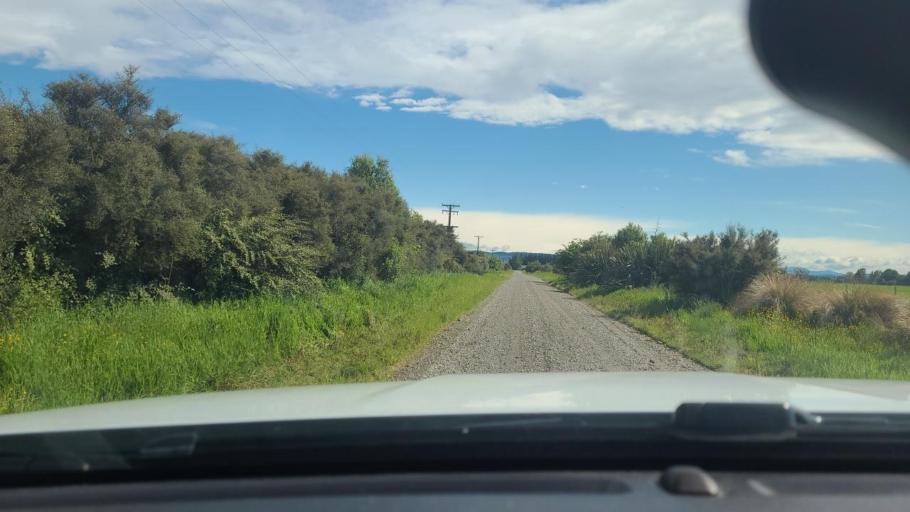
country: NZ
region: Southland
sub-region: Southland District
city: Winton
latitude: -46.0940
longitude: 168.2583
